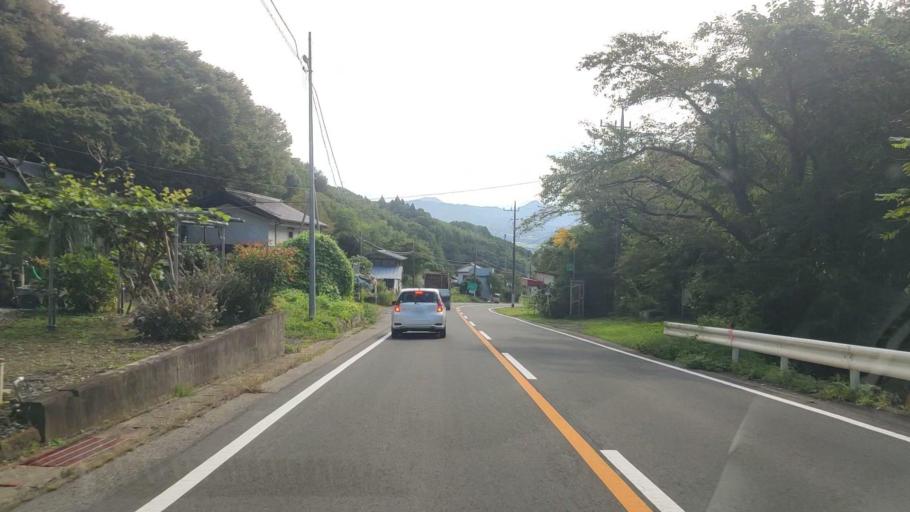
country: JP
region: Gunma
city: Numata
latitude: 36.6278
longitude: 139.0172
